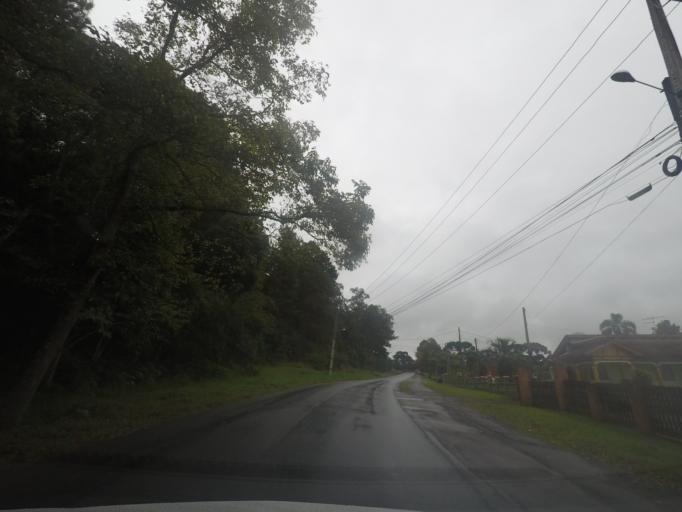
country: BR
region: Parana
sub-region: Quatro Barras
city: Quatro Barras
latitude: -25.3825
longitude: -49.1316
